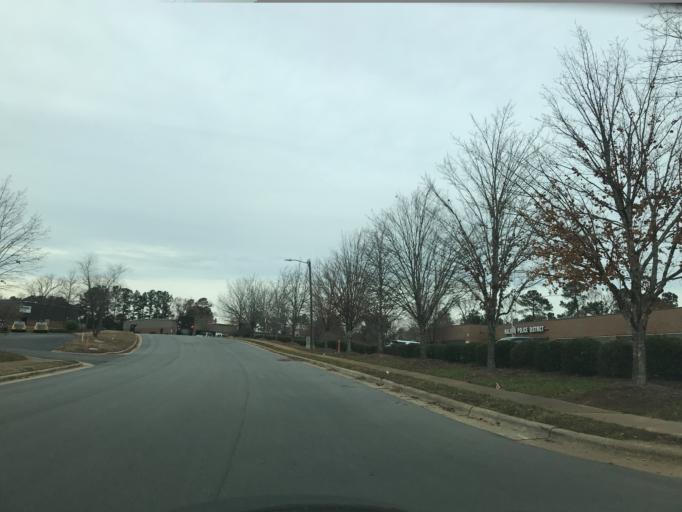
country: US
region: North Carolina
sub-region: Wake County
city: West Raleigh
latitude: 35.7913
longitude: -78.7018
